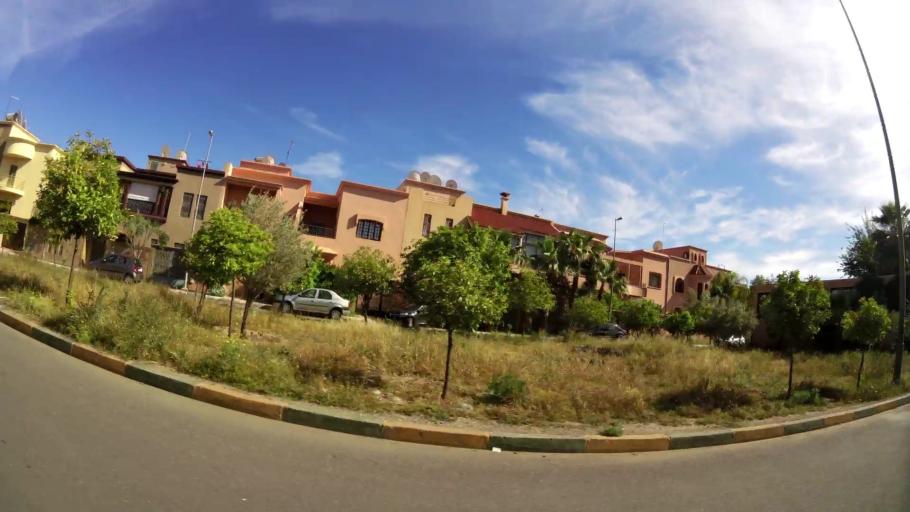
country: MA
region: Marrakech-Tensift-Al Haouz
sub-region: Marrakech
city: Marrakesh
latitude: 31.6511
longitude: -8.0466
